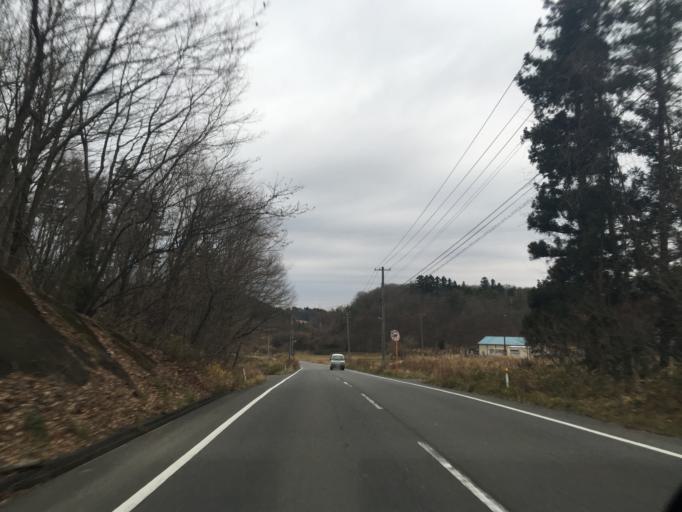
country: JP
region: Fukushima
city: Koriyama
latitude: 37.3536
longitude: 140.4466
